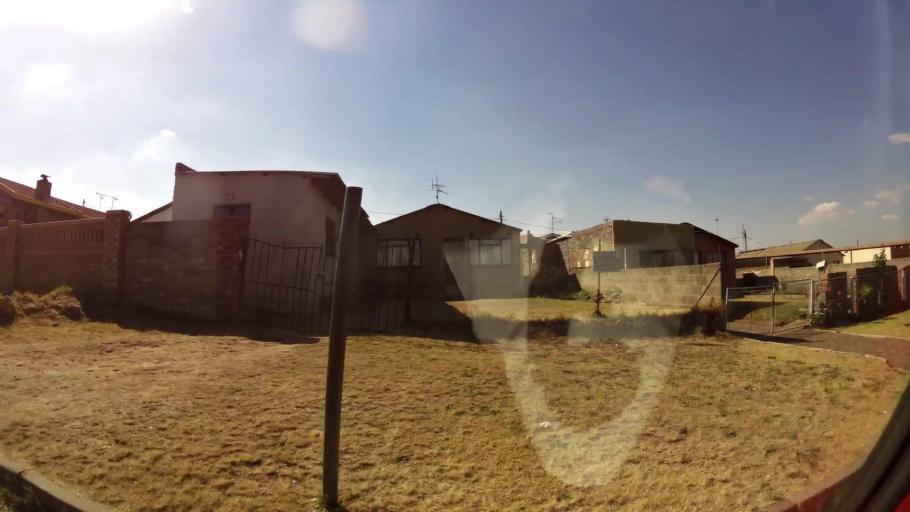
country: ZA
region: Gauteng
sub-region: City of Johannesburg Metropolitan Municipality
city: Soweto
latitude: -26.2441
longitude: 27.8980
